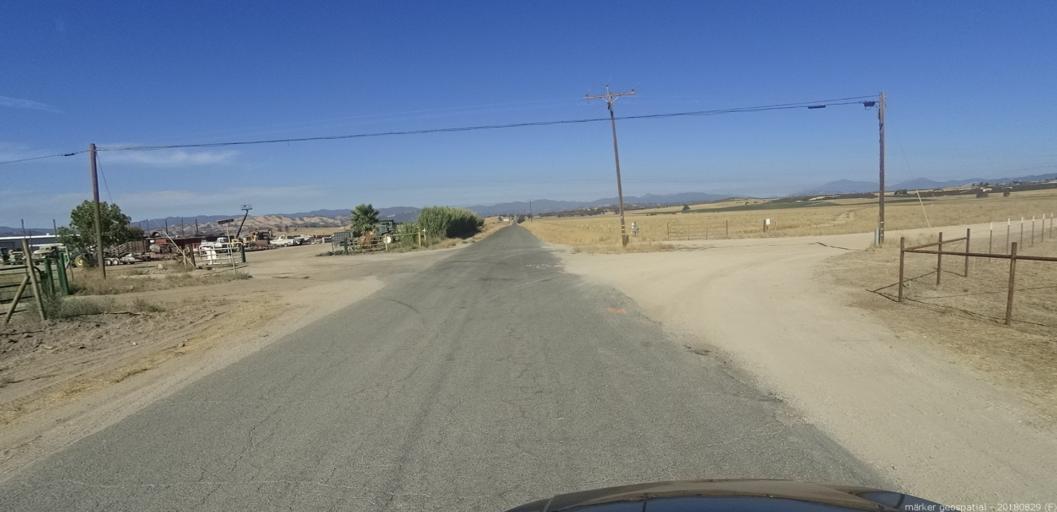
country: US
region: California
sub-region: Monterey County
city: King City
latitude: 35.9662
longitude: -121.0992
